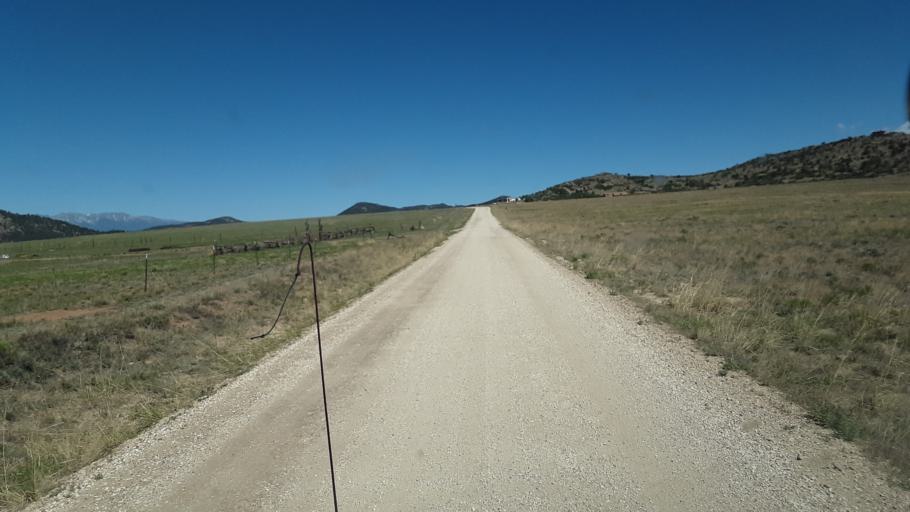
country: US
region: Colorado
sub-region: Custer County
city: Westcliffe
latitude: 38.2362
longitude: -105.4886
